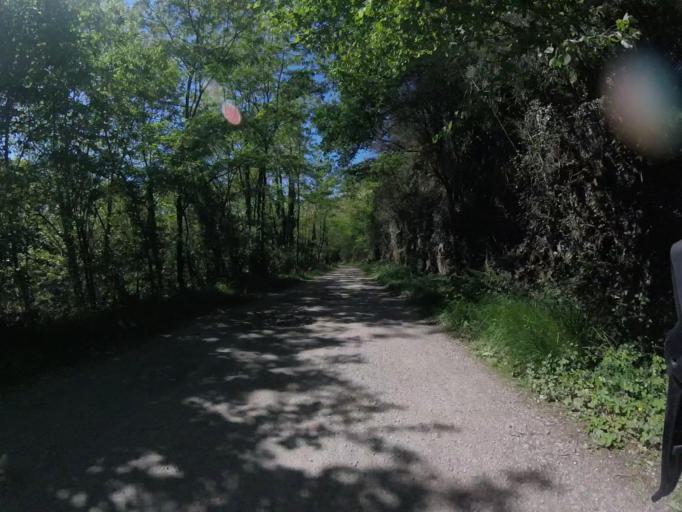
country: ES
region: Navarre
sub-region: Provincia de Navarra
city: Bera
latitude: 43.2834
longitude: -1.7137
